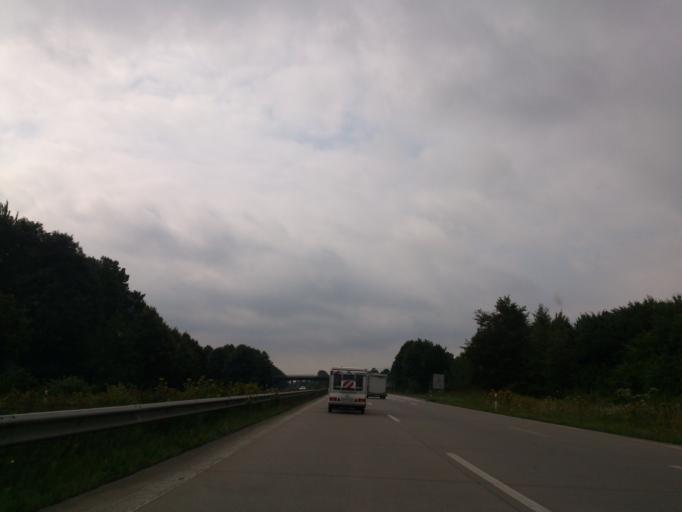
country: DE
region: Schleswig-Holstein
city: Kolln-Reisiek
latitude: 53.7471
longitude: 9.7113
